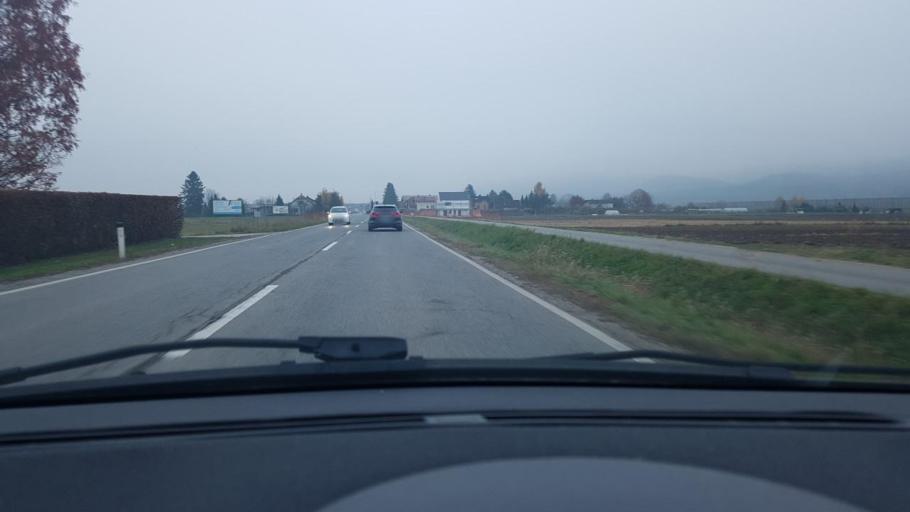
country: SI
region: Zalec
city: Zalec
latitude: 46.2432
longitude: 15.2083
